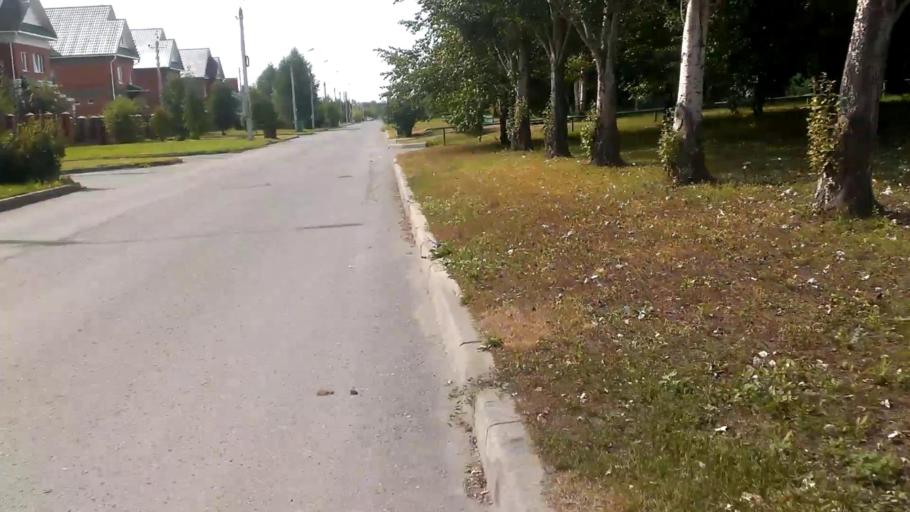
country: RU
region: Altai Krai
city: Novosilikatnyy
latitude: 53.3555
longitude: 83.6534
